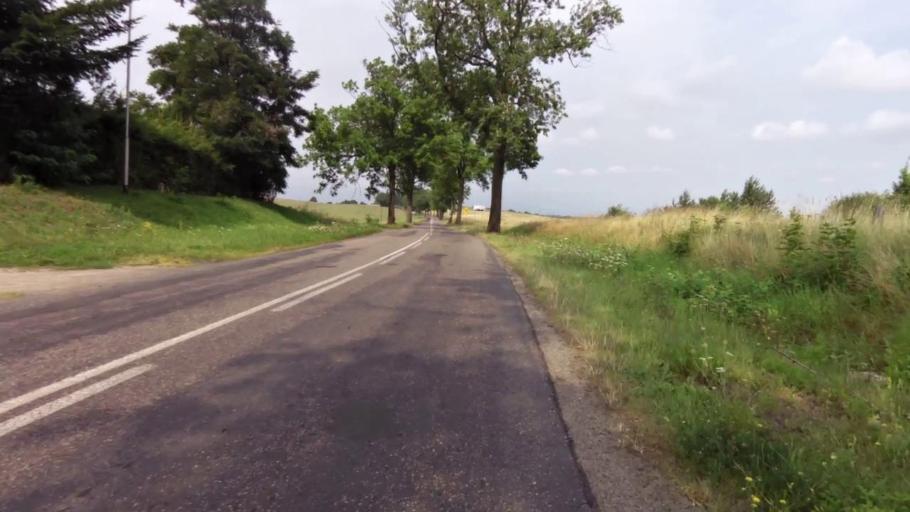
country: PL
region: West Pomeranian Voivodeship
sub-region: Powiat drawski
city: Drawsko Pomorskie
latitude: 53.5539
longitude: 15.8249
